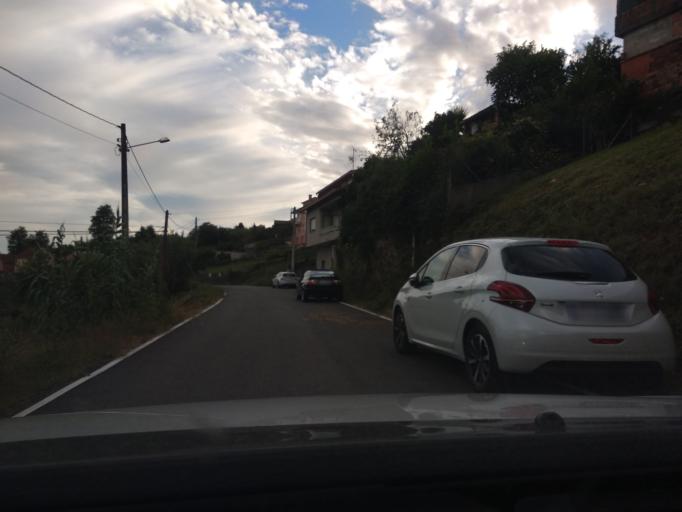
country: ES
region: Galicia
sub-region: Provincia de Pontevedra
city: Moana
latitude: 42.2978
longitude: -8.7387
